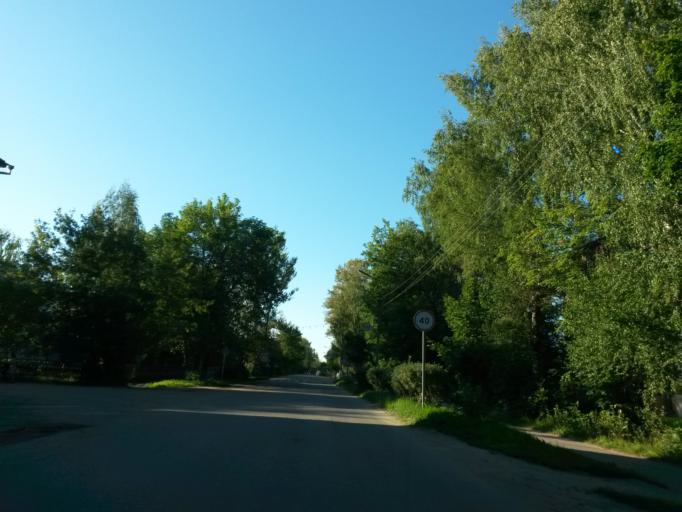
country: RU
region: Jaroslavl
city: Gavrilov-Yam
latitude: 57.3015
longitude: 39.8634
